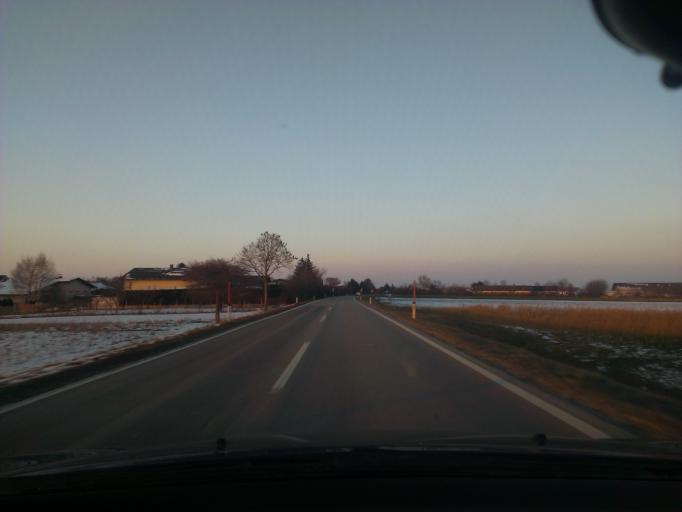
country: AT
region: Lower Austria
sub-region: Politischer Bezirk Baden
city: Reisenberg
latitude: 47.9894
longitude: 16.5187
